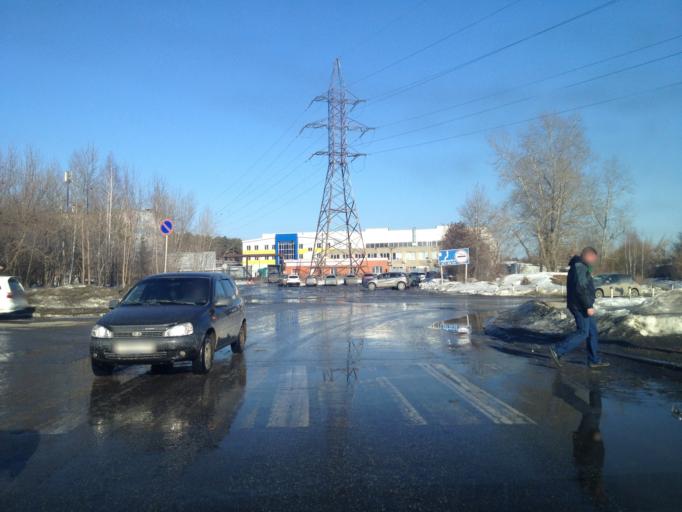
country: RU
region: Sverdlovsk
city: Yekaterinburg
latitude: 56.9121
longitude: 60.6280
